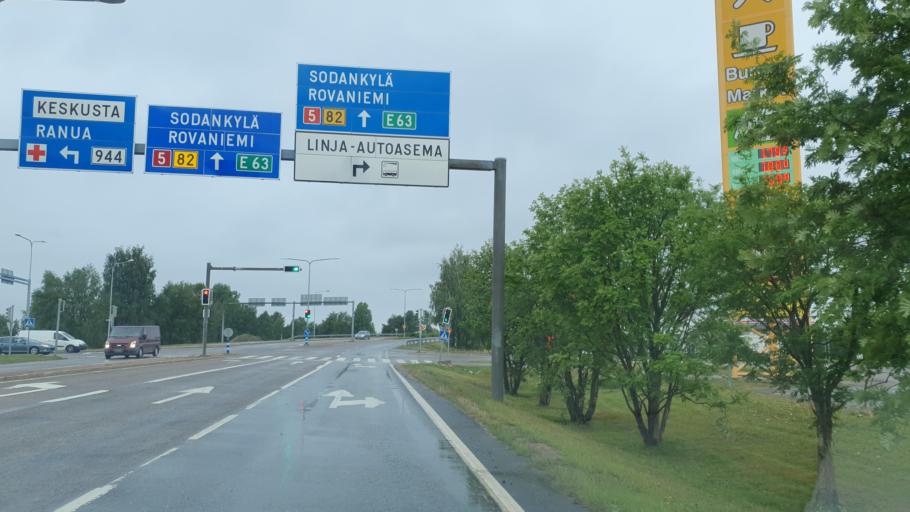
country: FI
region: Lapland
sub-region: Itae-Lappi
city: Kemijaervi
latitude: 66.7170
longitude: 27.4282
